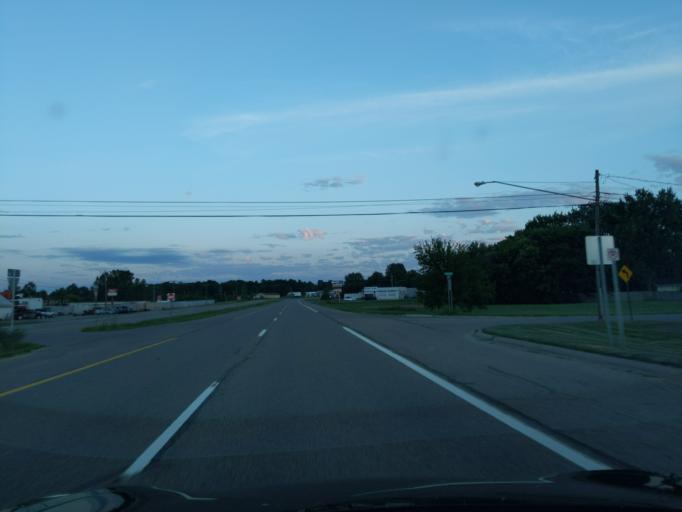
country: US
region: Michigan
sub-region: Clinton County
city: Saint Johns
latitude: 43.0125
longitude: -84.5560
